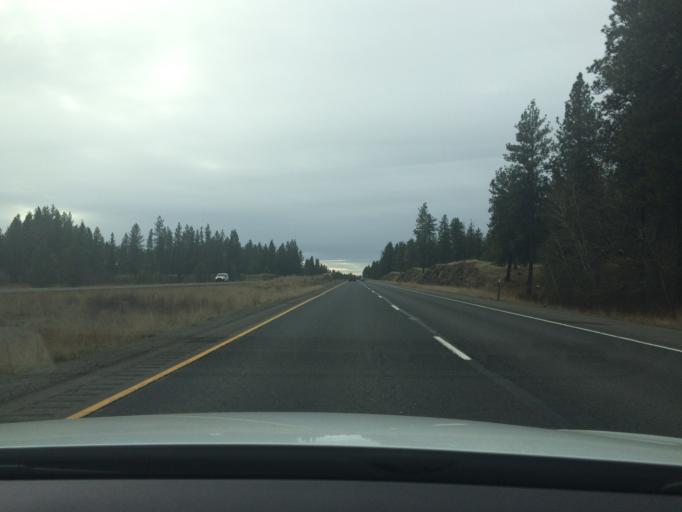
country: US
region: Washington
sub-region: Spokane County
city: Medical Lake
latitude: 47.5224
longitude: -117.6662
